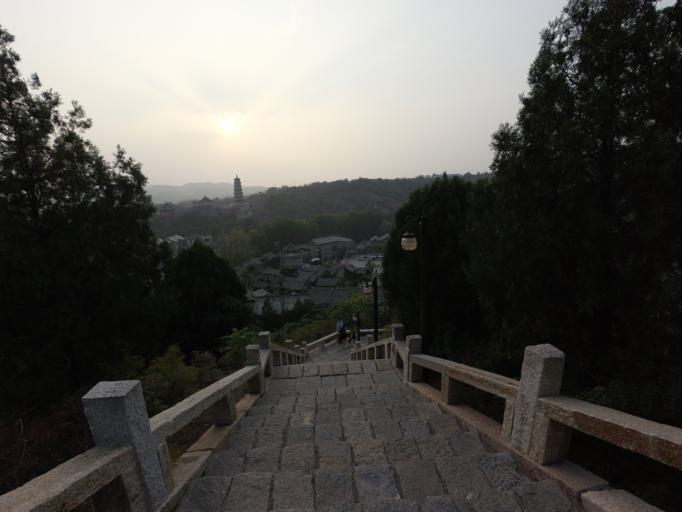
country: CN
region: Beijing
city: Xinchengzi
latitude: 40.6499
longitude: 117.2686
